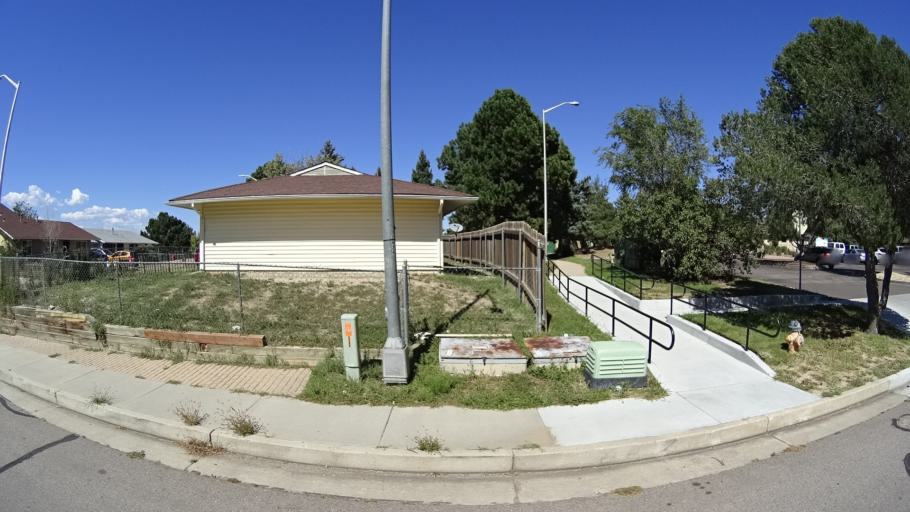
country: US
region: Colorado
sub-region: El Paso County
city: Stratmoor
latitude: 38.7841
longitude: -104.7486
